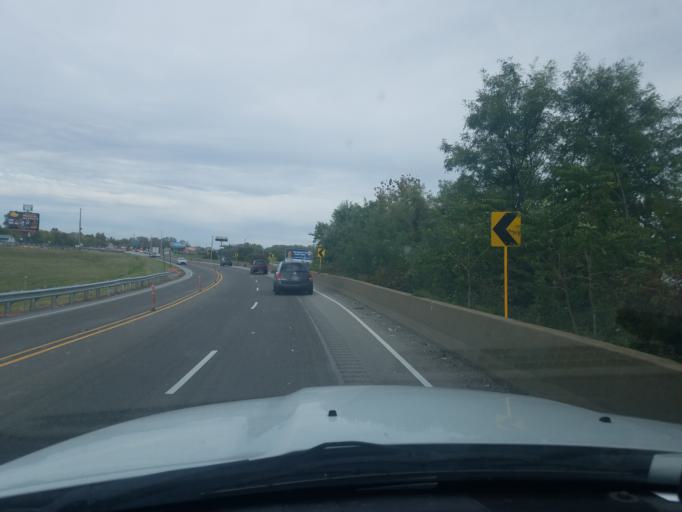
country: US
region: Indiana
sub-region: Vanderburgh County
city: Evansville
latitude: 37.9122
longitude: -87.5478
